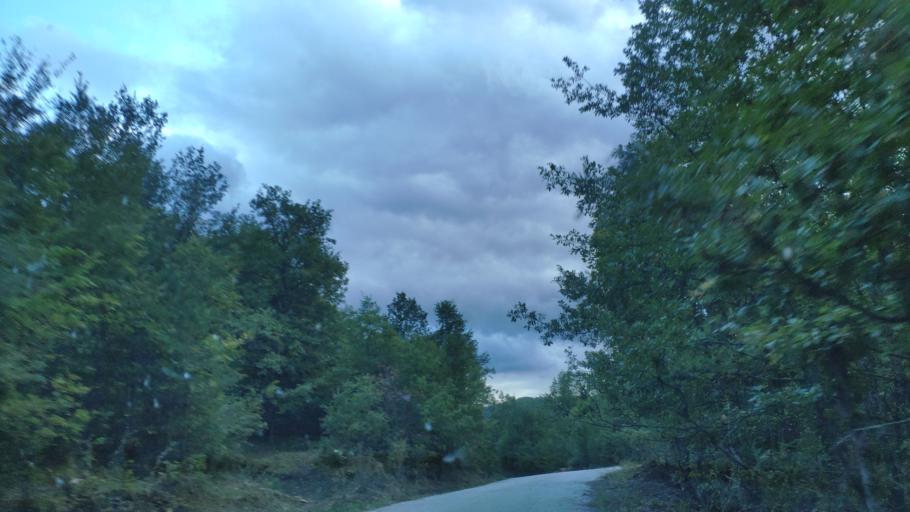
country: AL
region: Korce
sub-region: Rrethi i Kolonjes
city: Erseke
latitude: 40.2603
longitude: 20.8581
